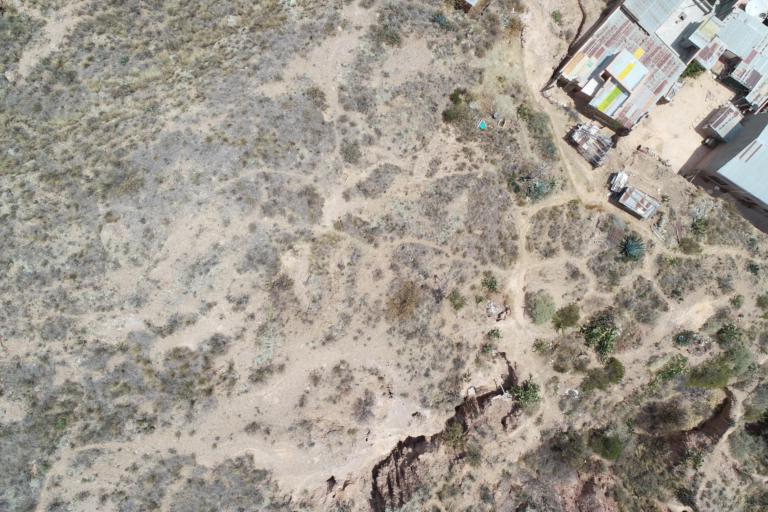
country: BO
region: La Paz
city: La Paz
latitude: -16.5584
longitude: -68.0920
